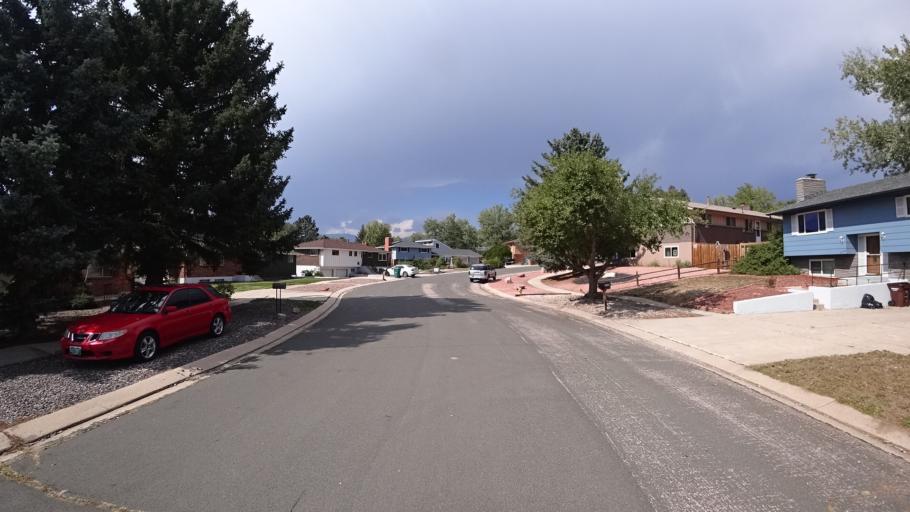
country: US
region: Colorado
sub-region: El Paso County
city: Cimarron Hills
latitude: 38.8643
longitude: -104.7601
